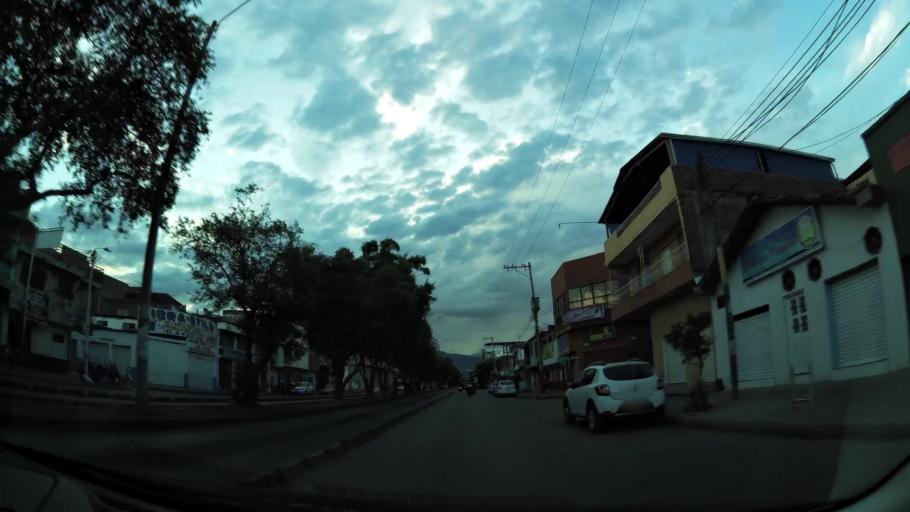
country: CO
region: Valle del Cauca
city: Cali
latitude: 3.4446
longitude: -76.5041
